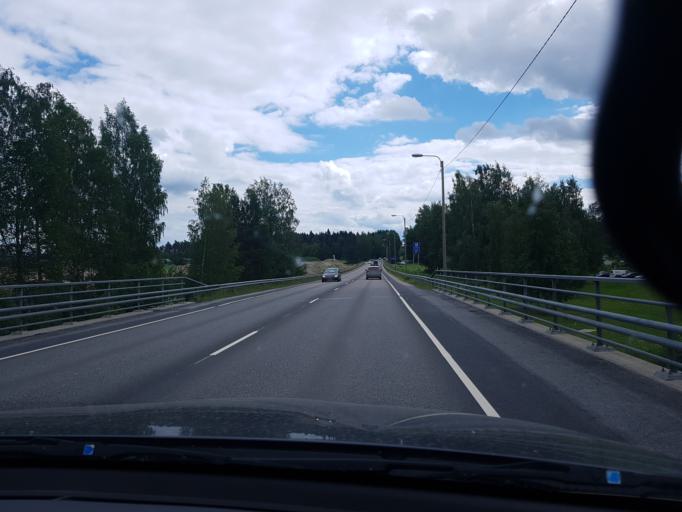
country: FI
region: Pirkanmaa
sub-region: Tampere
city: Paelkaene
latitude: 61.3365
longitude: 24.2804
